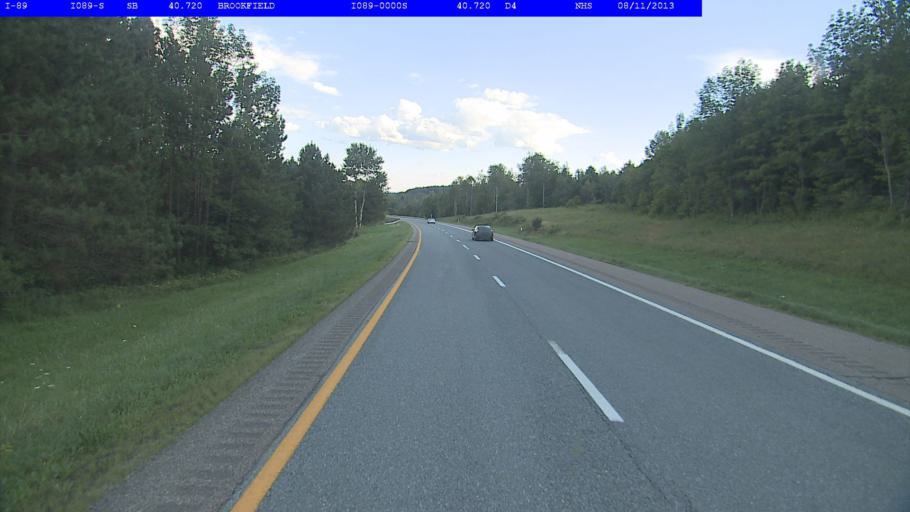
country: US
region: Vermont
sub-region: Washington County
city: Northfield
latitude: 44.0838
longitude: -72.6149
